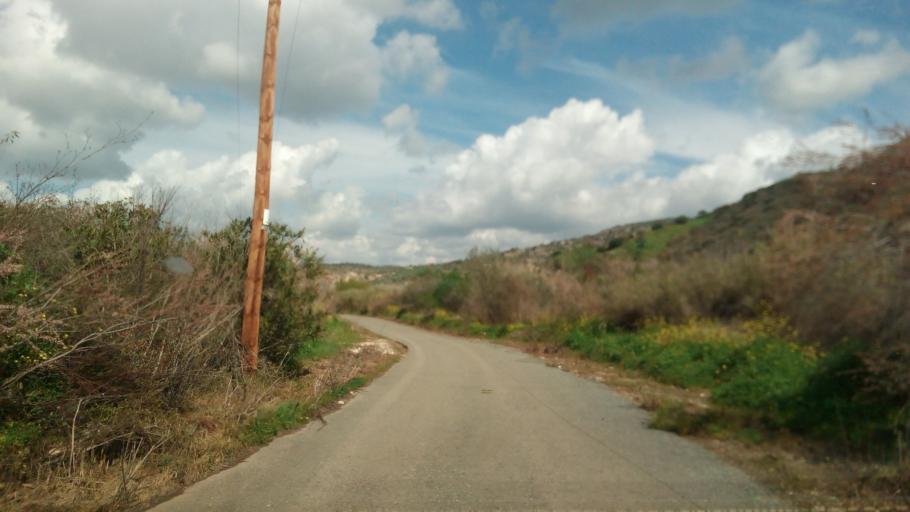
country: CY
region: Pafos
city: Mesogi
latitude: 34.7990
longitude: 32.5289
